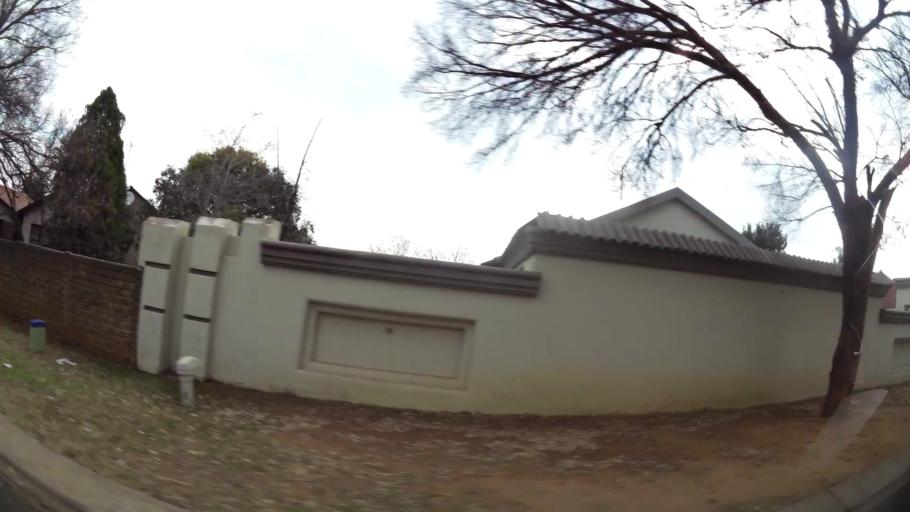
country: ZA
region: Gauteng
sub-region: Ekurhuleni Metropolitan Municipality
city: Benoni
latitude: -26.1270
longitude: 28.3615
